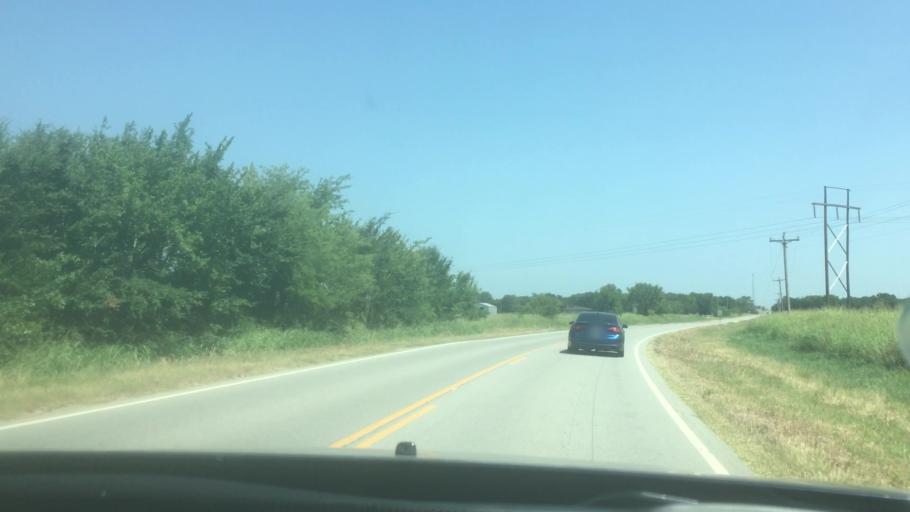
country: US
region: Oklahoma
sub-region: Coal County
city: Coalgate
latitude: 34.5941
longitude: -96.4243
